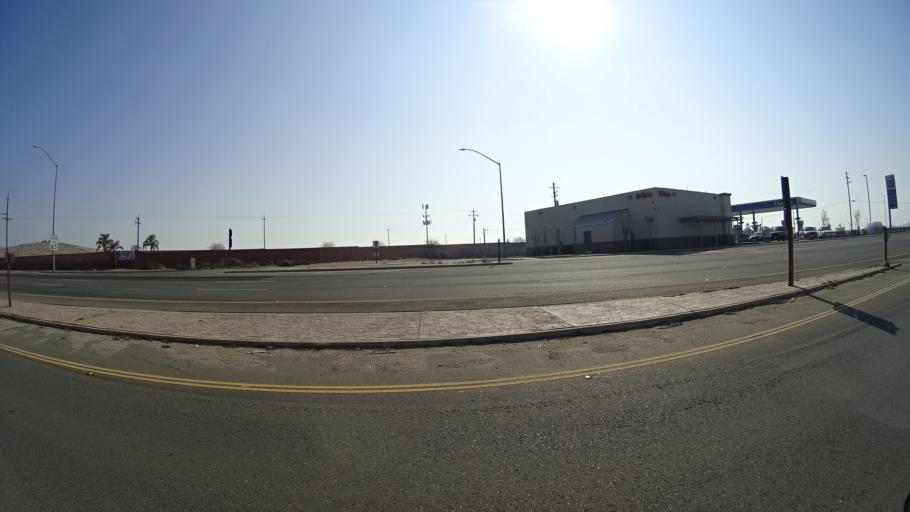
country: US
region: California
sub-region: Kern County
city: Bakersfield
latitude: 35.3986
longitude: -118.8800
